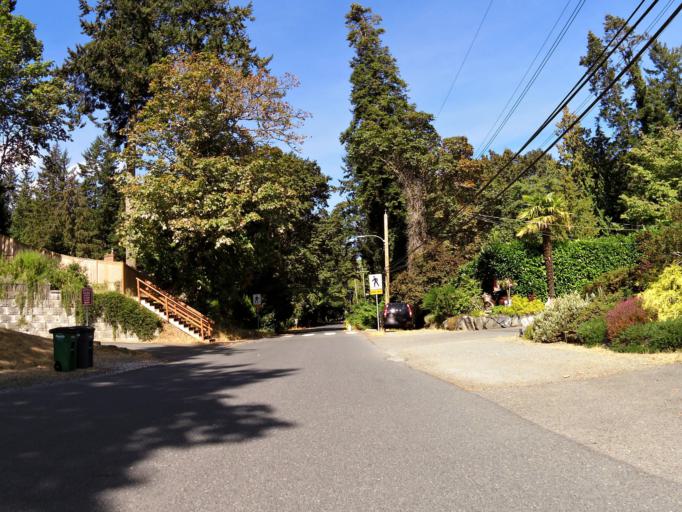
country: CA
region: British Columbia
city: Victoria
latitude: 48.5223
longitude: -123.3718
